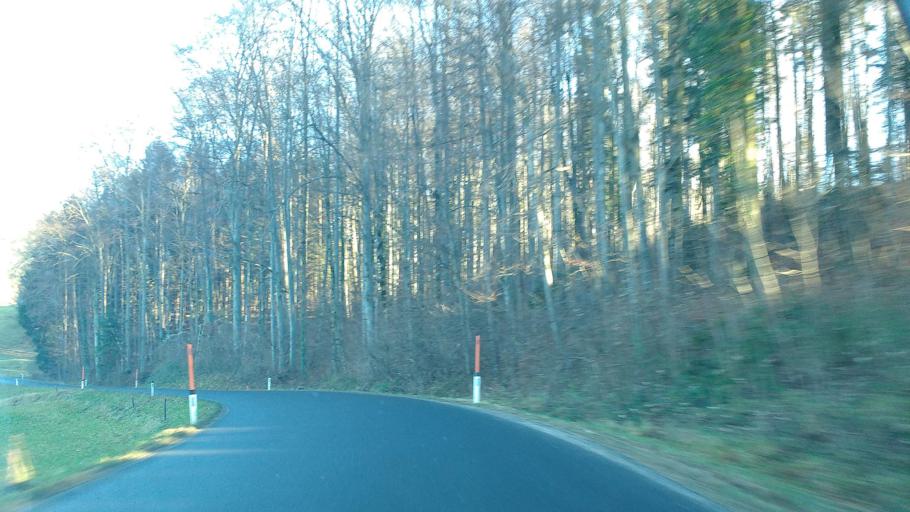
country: AT
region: Upper Austria
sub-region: Politischer Bezirk Kirchdorf an der Krems
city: Micheldorf in Oberoesterreich
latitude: 47.9074
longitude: 14.1355
